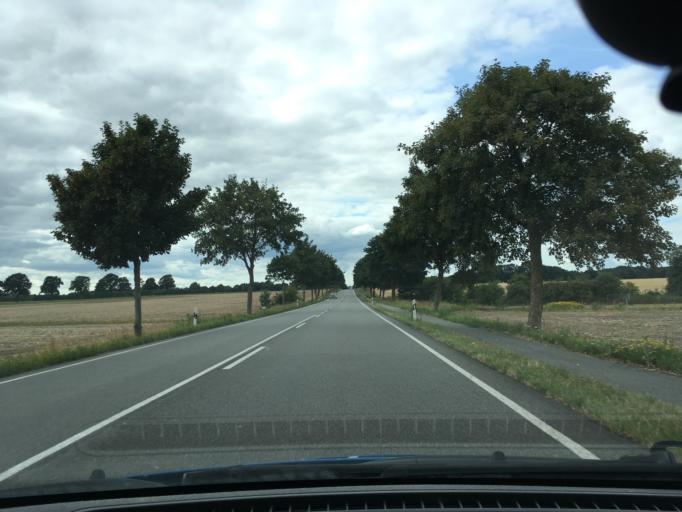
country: DE
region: Lower Saxony
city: Neu Wulmstorf
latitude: 53.4366
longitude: 9.7701
